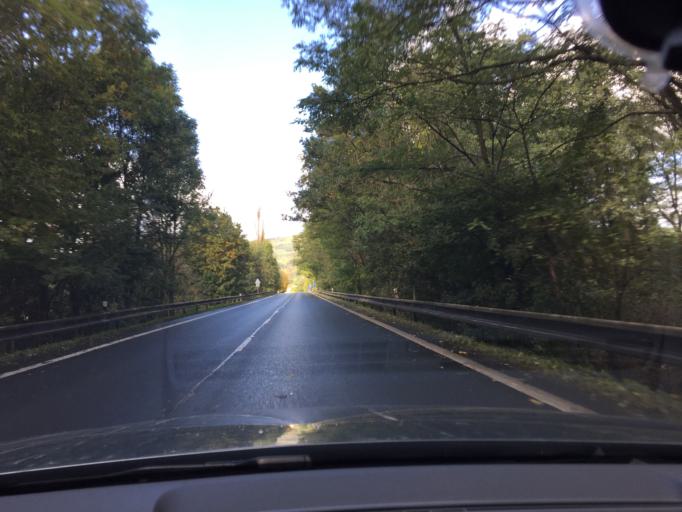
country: CZ
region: Ustecky
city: Chlumec
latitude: 50.6914
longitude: 13.9444
